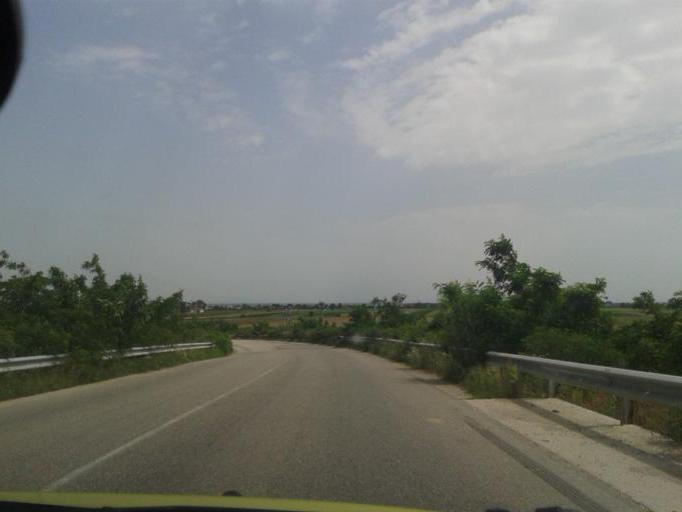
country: RO
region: Dambovita
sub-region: Comuna Petresti
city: Petresti
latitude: 44.6680
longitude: 25.3083
